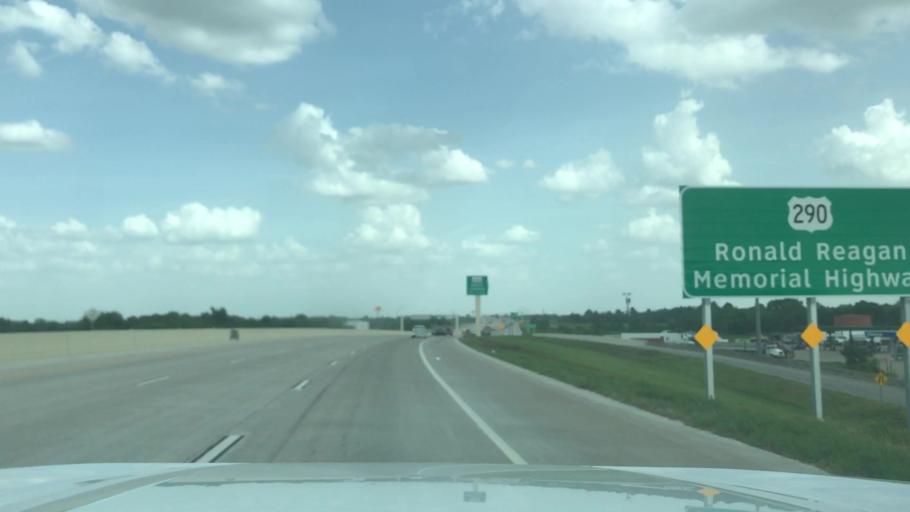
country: US
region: Texas
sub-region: Waller County
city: Waller
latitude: 30.0686
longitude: -95.9210
